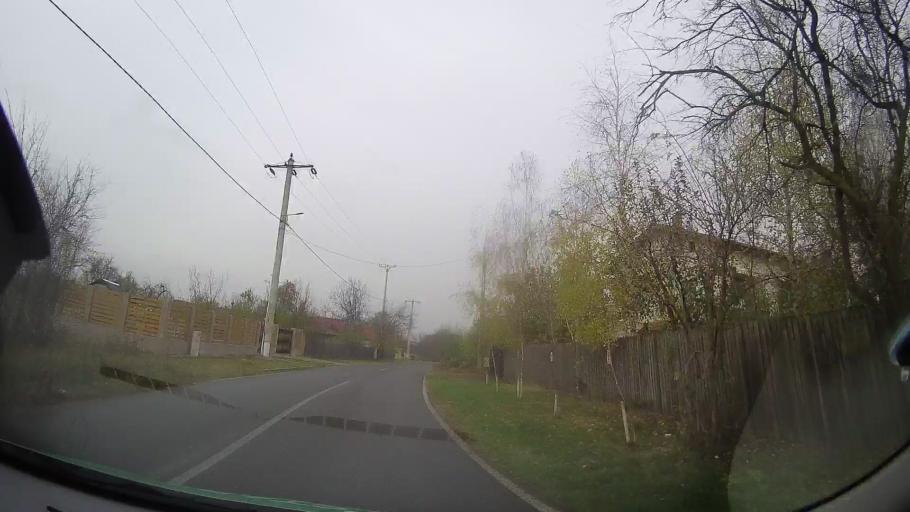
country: RO
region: Ilfov
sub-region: Comuna Gruiu
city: Gruiu
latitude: 44.7252
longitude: 26.2135
